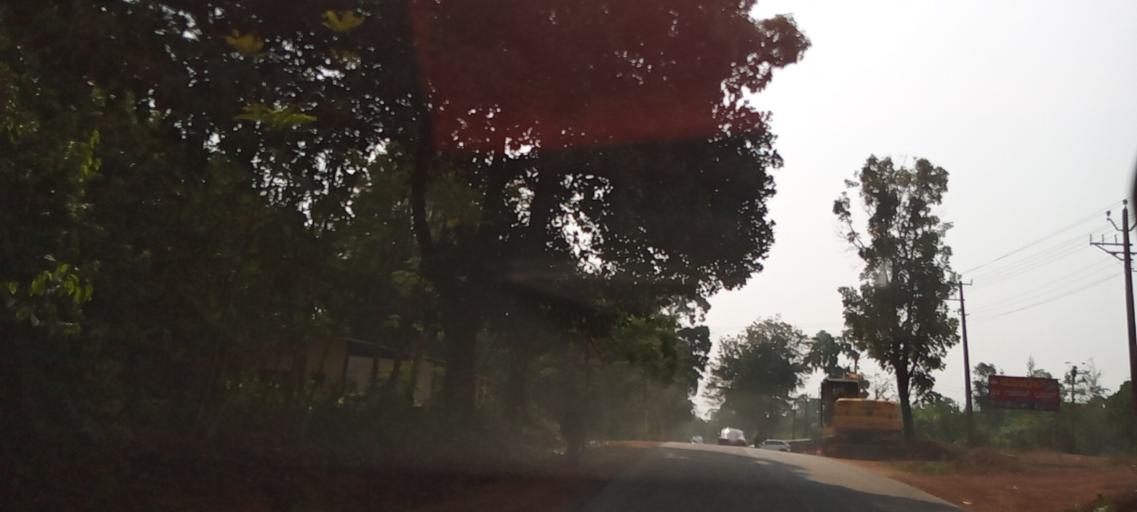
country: IN
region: Karnataka
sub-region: Udupi
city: Someshwar
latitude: 13.5314
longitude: 74.9185
